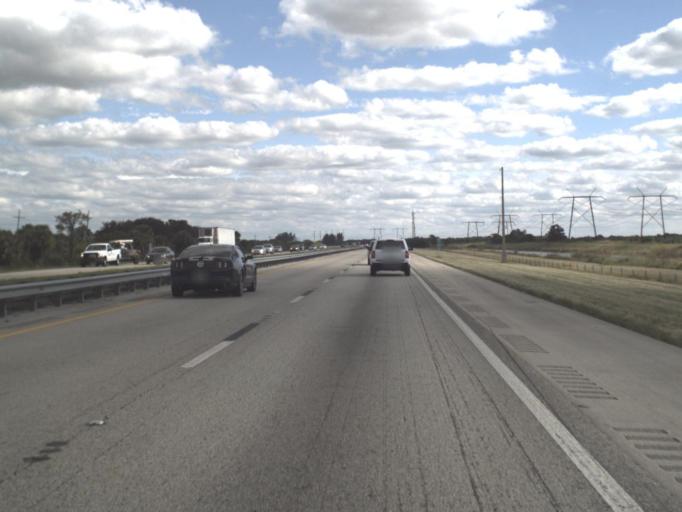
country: US
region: Florida
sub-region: Indian River County
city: West Vero Corridor
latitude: 27.4987
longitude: -80.5792
